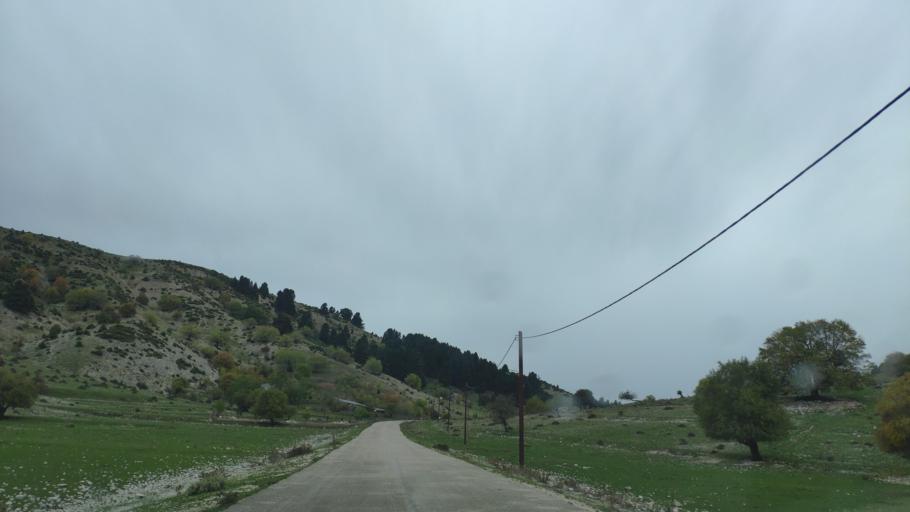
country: GR
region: Epirus
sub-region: Nomos Thesprotias
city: Paramythia
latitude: 39.4487
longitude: 20.6463
